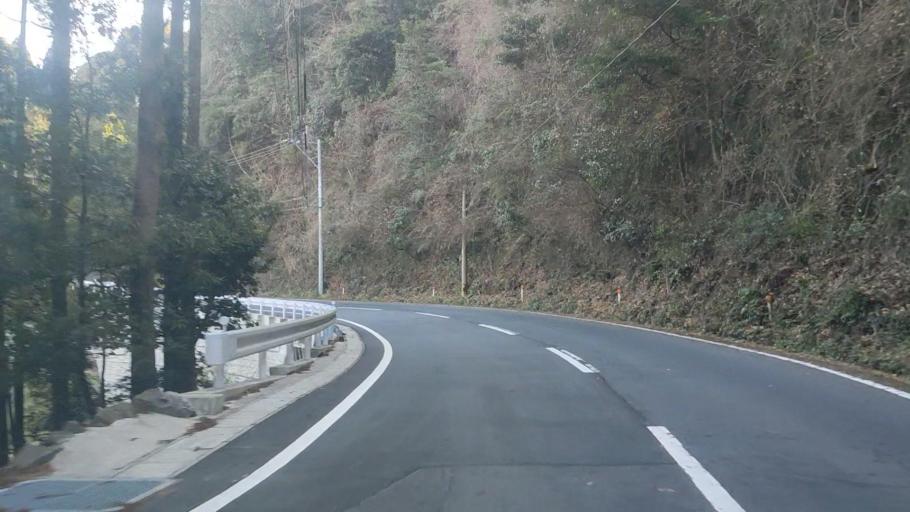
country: JP
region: Kagoshima
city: Kokubu-matsuki
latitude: 31.6684
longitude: 130.8386
